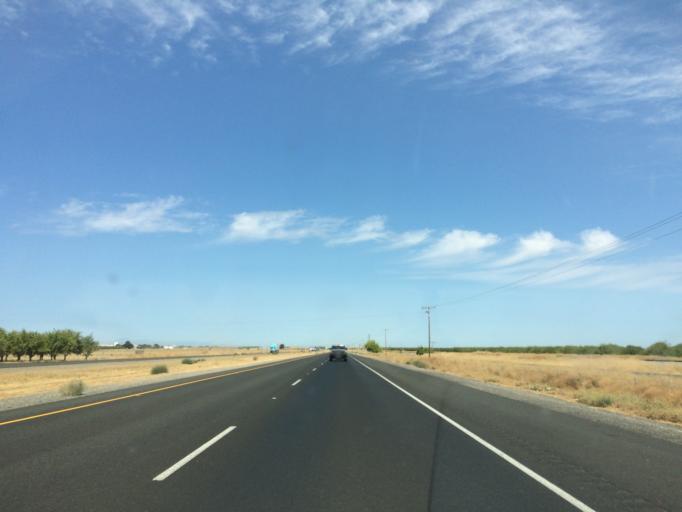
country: US
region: California
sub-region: Yolo County
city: Dunnigan
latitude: 38.9390
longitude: -122.0056
